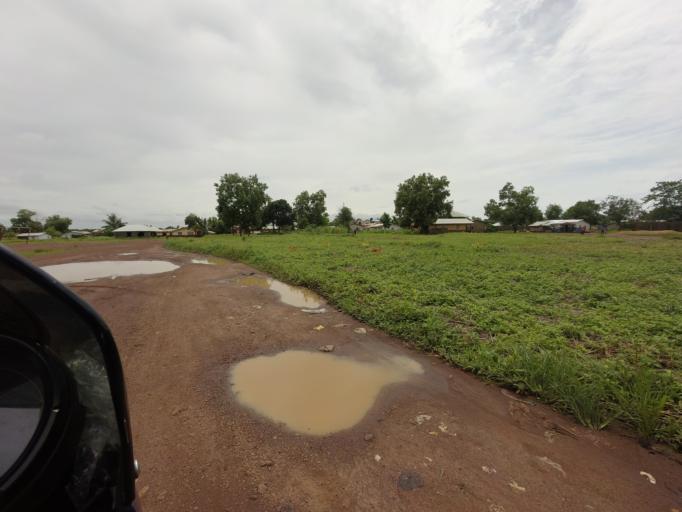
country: SL
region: Northern Province
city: Kambia
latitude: 9.1047
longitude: -12.9242
